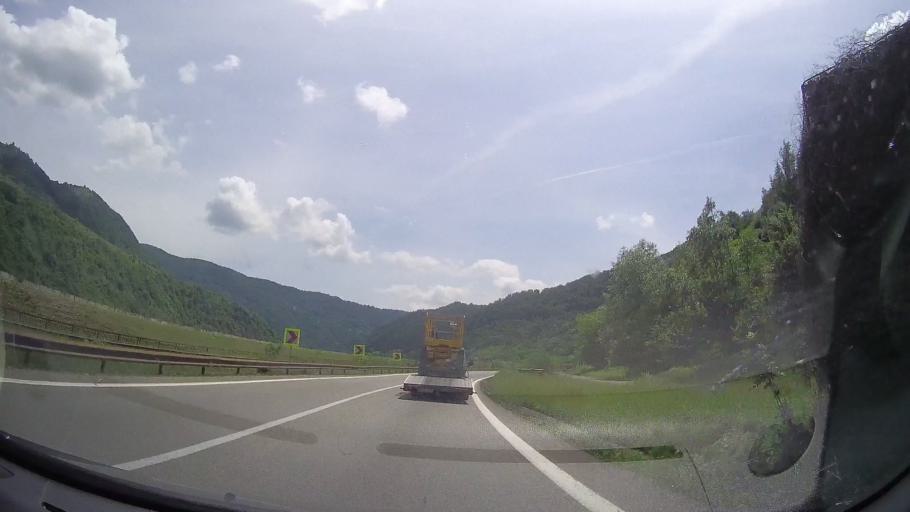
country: RO
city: Cainenii Mici
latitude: 45.4616
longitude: 24.2874
